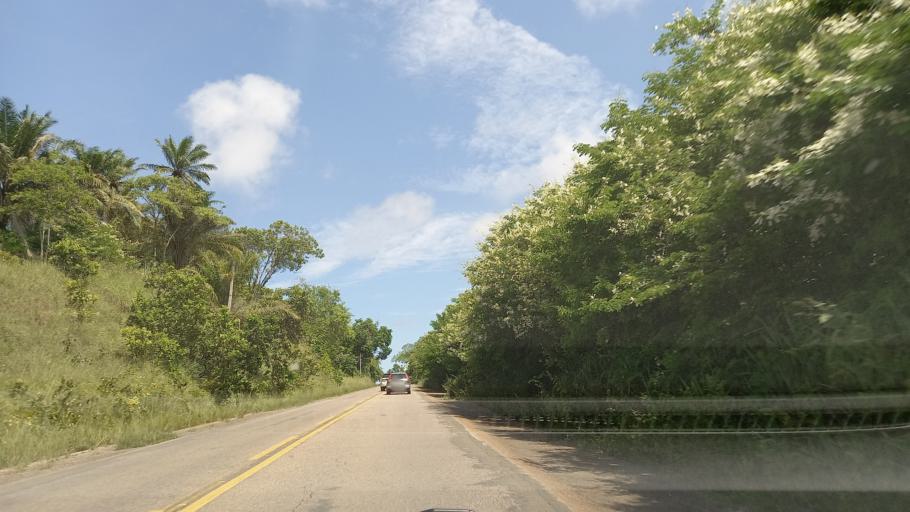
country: BR
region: Pernambuco
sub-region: Barreiros
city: Barreiros
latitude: -8.8549
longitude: -35.1675
